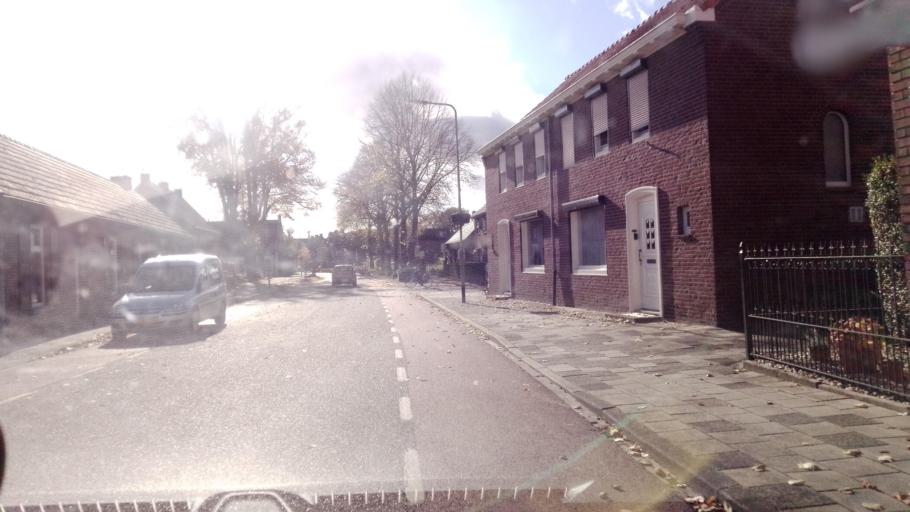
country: NL
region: Limburg
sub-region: Gemeente Venlo
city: Venlo
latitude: 51.4218
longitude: 6.1474
